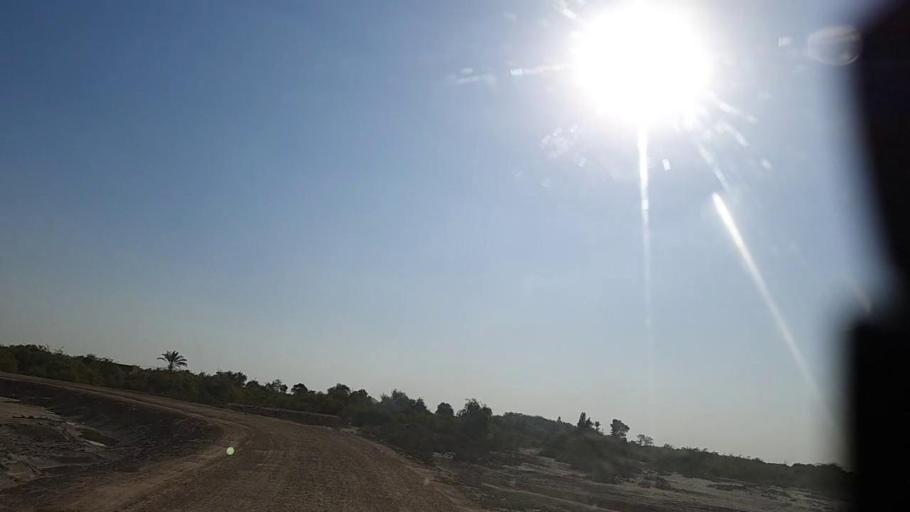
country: PK
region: Sindh
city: Digri
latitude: 25.1493
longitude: 69.0369
